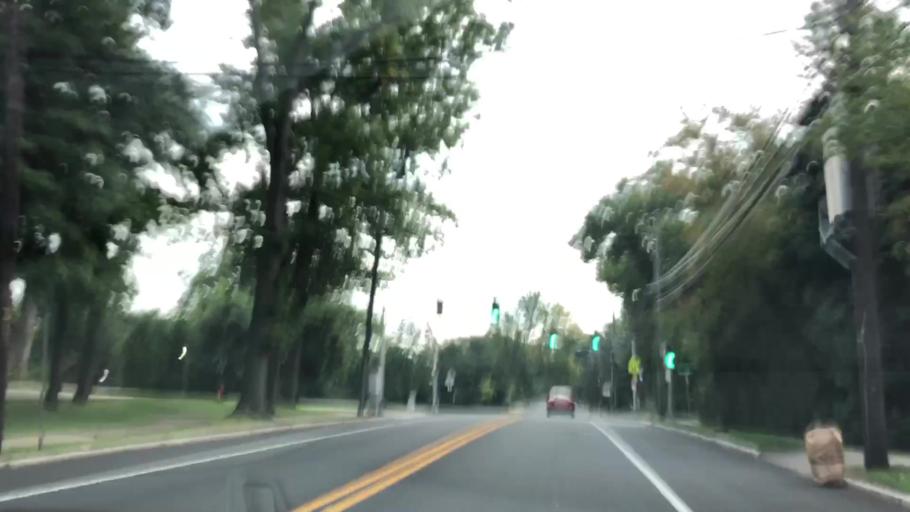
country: US
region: New Jersey
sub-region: Essex County
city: Upper Montclair
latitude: 40.8461
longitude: -74.1944
